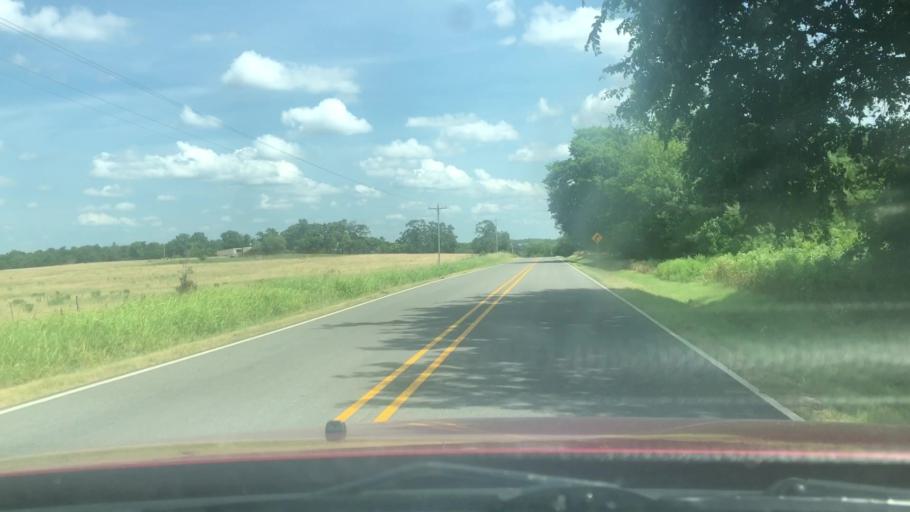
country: US
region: Arkansas
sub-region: Carroll County
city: Berryville
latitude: 36.3974
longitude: -93.5478
